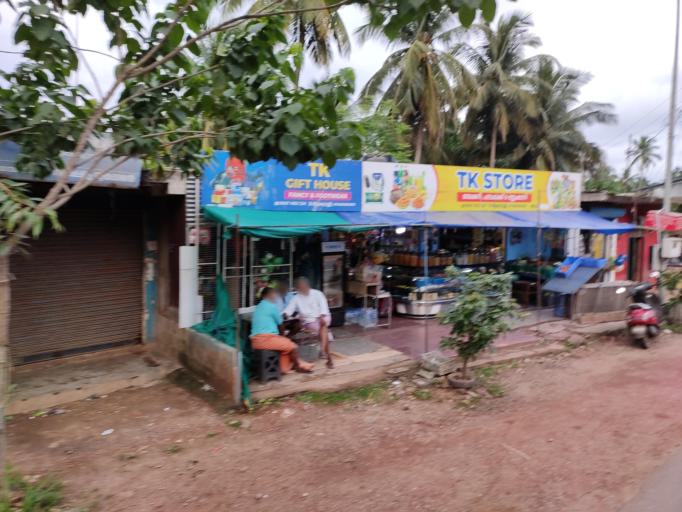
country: IN
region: Kerala
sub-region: Palakkad district
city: Mannarakkat
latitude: 10.9845
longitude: 76.4831
